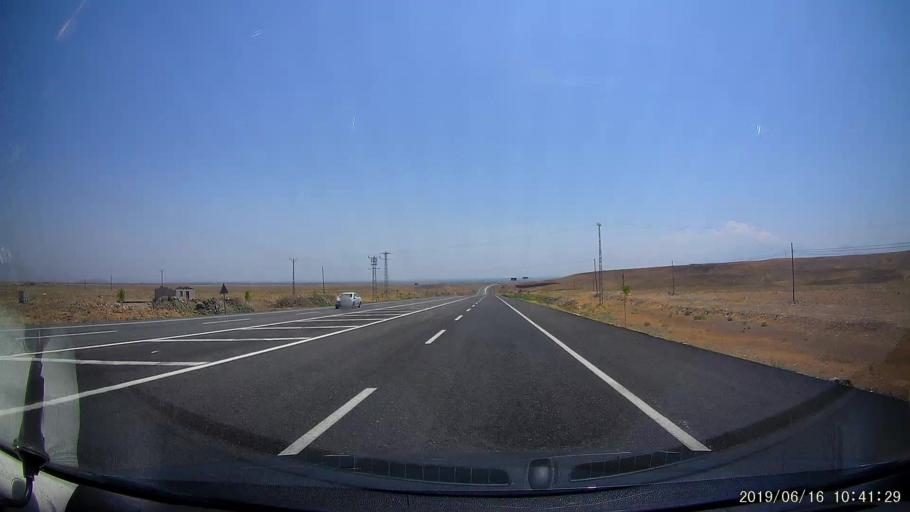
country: TR
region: Igdir
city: Tuzluca
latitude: 40.0472
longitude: 43.7842
